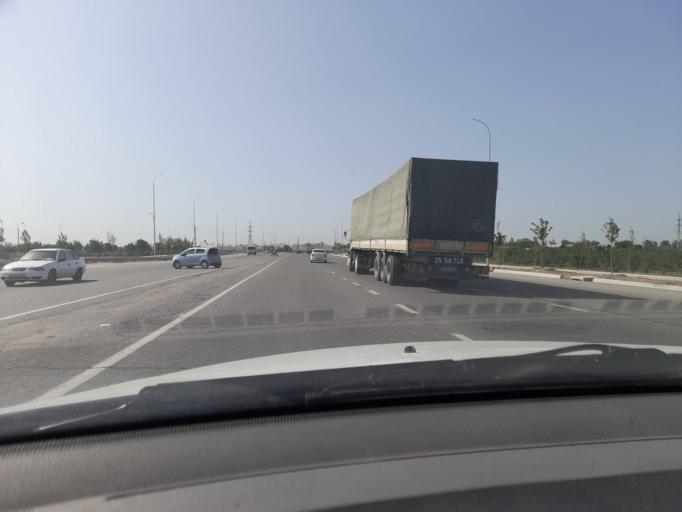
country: UZ
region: Samarqand
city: Daxbet
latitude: 39.7379
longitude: 66.9300
